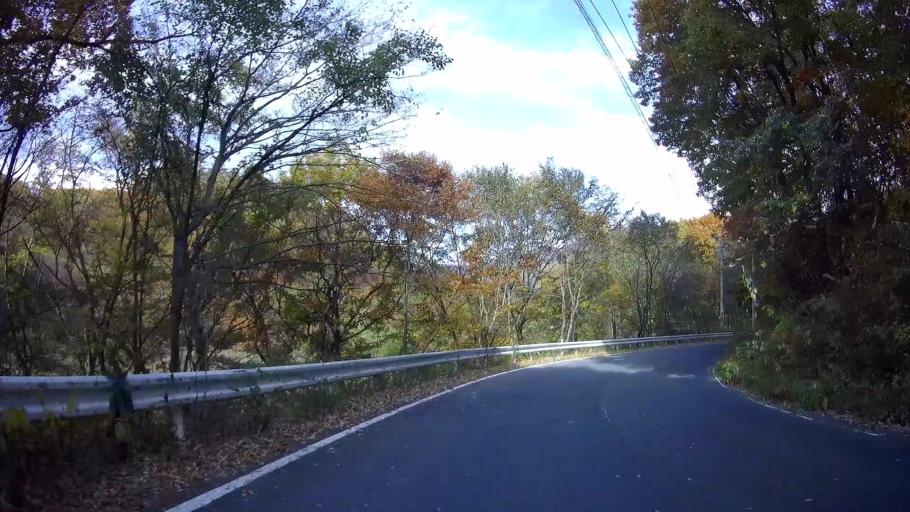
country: JP
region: Gunma
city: Nakanojomachi
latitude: 36.5373
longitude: 138.6528
